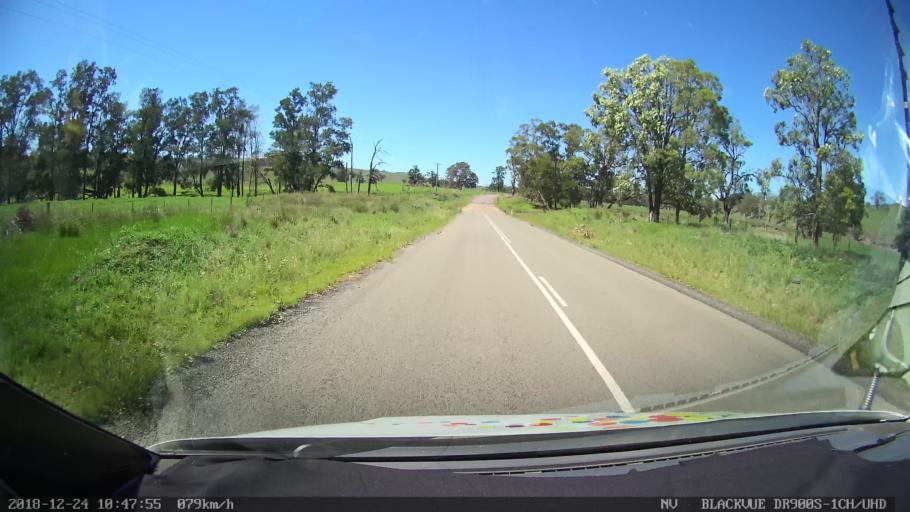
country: AU
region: New South Wales
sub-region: Upper Hunter Shire
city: Merriwa
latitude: -31.9302
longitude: 150.4298
